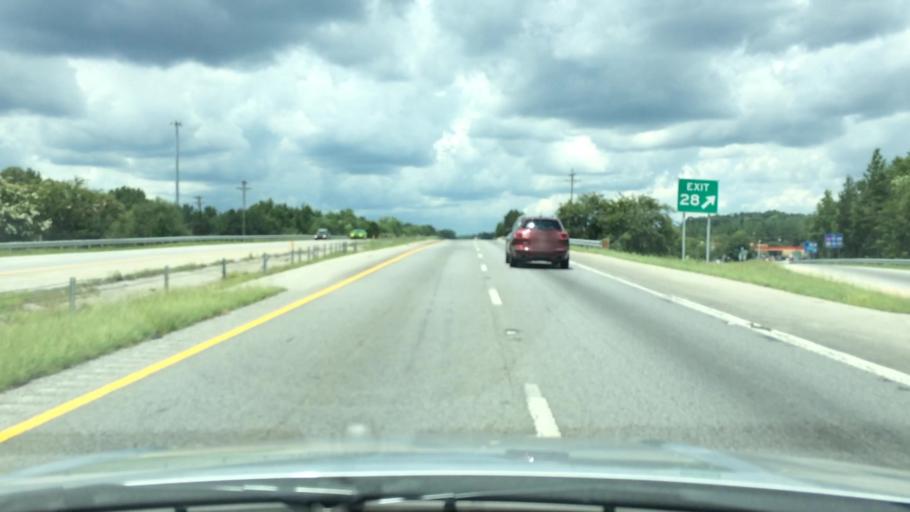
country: US
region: South Carolina
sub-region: Spartanburg County
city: Roebuck
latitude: 34.8363
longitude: -81.9699
